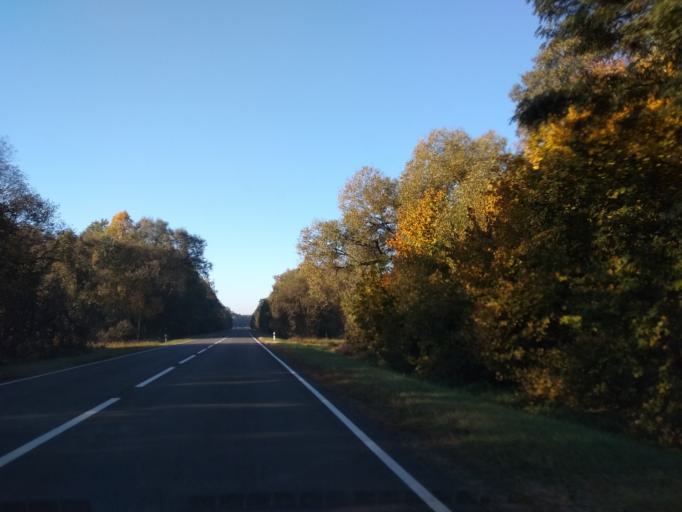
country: BY
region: Brest
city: Kobryn
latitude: 52.0195
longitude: 24.2408
